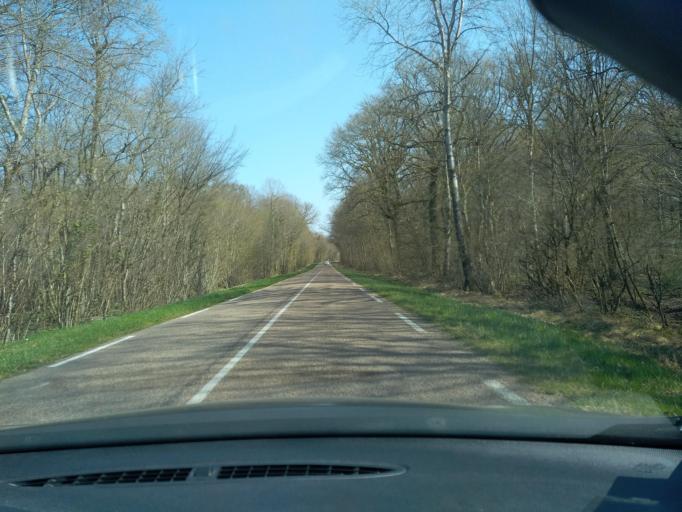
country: FR
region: Franche-Comte
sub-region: Departement du Jura
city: Mont-sous-Vaudrey
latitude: 46.9558
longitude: 5.5286
